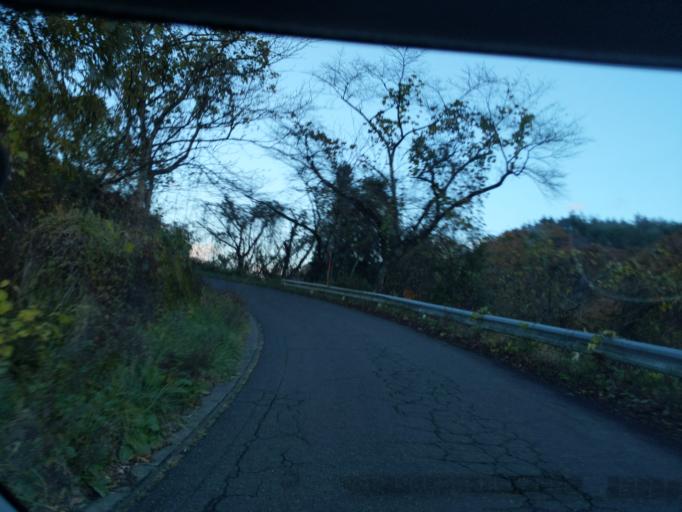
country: JP
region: Iwate
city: Ichinoseki
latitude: 39.0091
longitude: 141.0601
